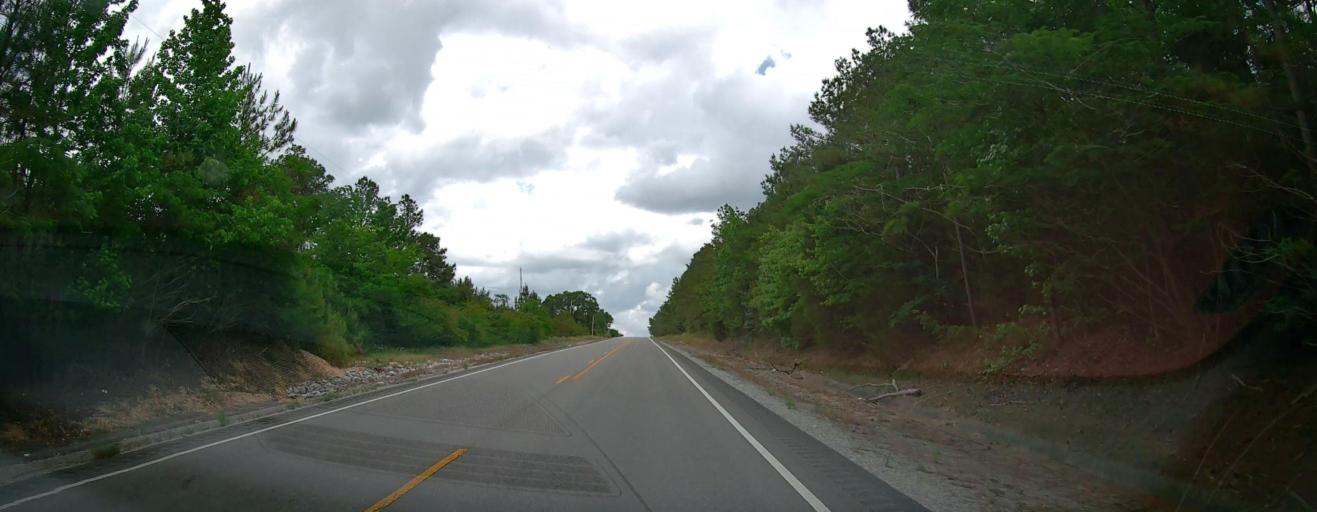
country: US
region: Alabama
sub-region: Marion County
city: Hamilton
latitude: 34.1311
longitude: -88.0259
